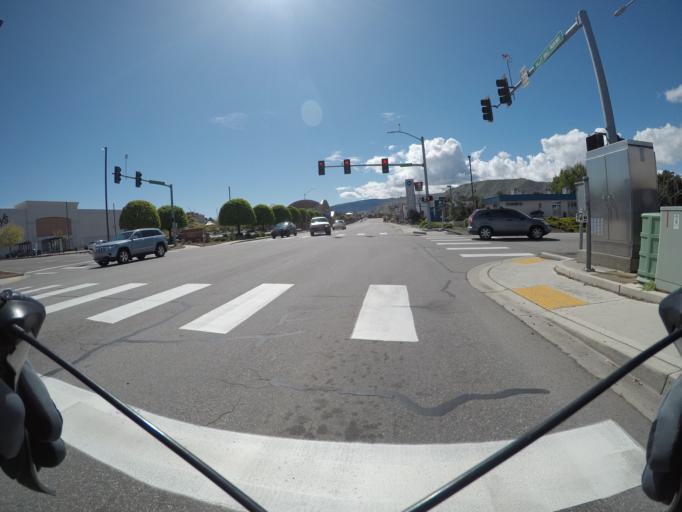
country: US
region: Washington
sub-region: Douglas County
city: East Wenatchee
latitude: 47.4108
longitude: -120.2903
